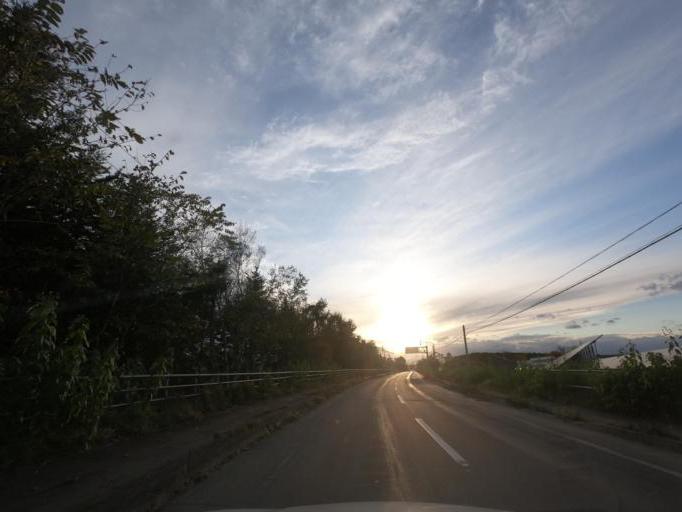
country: JP
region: Hokkaido
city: Obihiro
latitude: 42.5673
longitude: 143.3141
